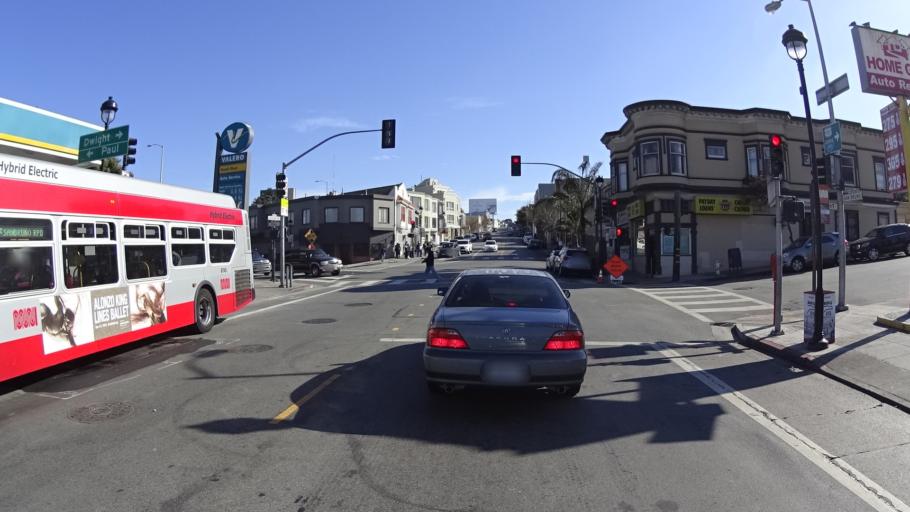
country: US
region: California
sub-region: San Mateo County
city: Brisbane
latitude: 37.7242
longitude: -122.4022
